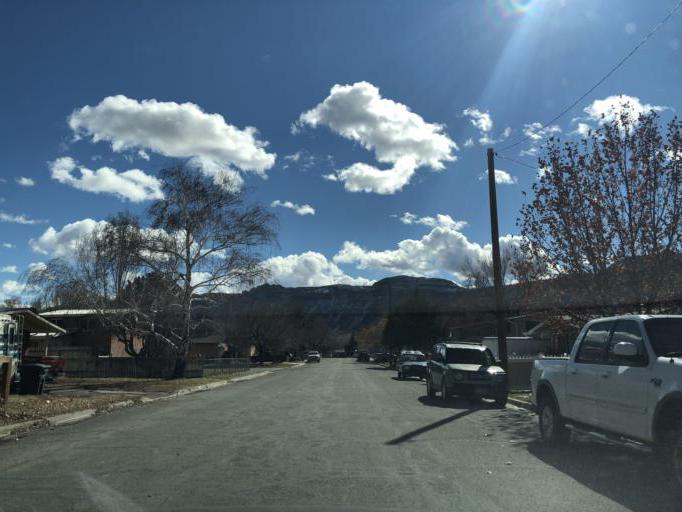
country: US
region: Utah
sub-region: Grand County
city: Moab
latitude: 38.5816
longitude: -109.5596
